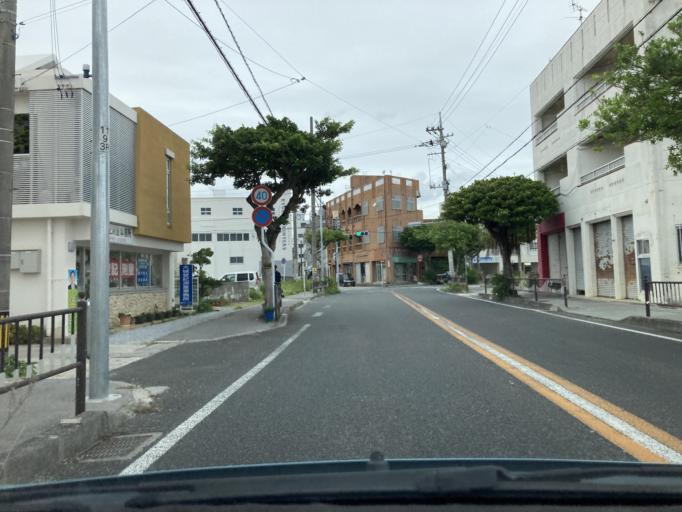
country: JP
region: Okinawa
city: Itoman
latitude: 26.1276
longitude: 127.6689
